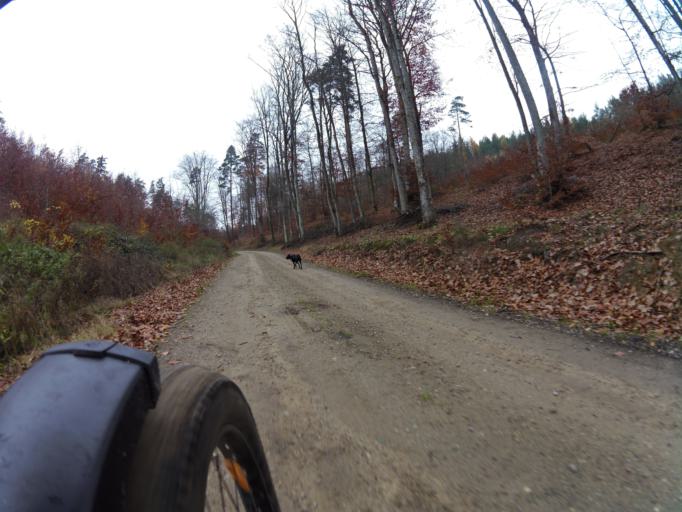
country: PL
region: Pomeranian Voivodeship
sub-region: Powiat pucki
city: Krokowa
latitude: 54.7127
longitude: 18.1424
